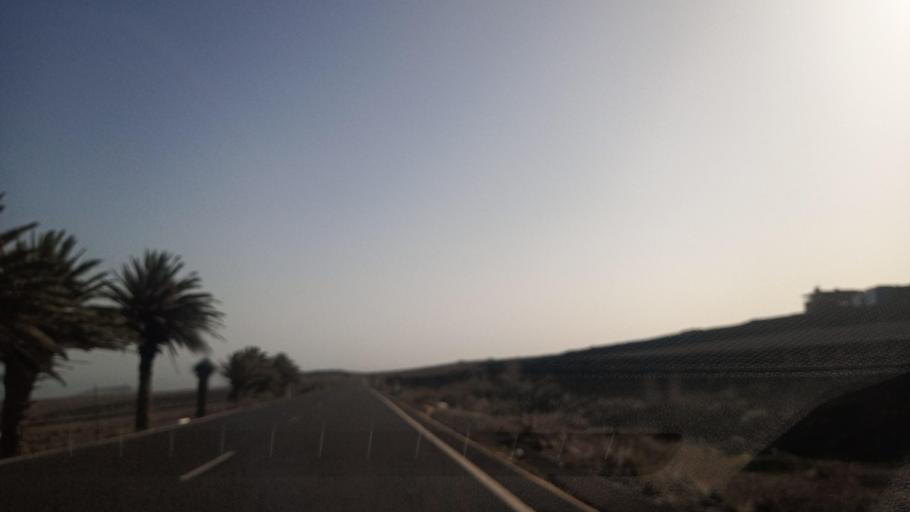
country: ES
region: Canary Islands
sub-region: Provincia de Las Palmas
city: Haria
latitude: 29.1203
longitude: -13.5153
